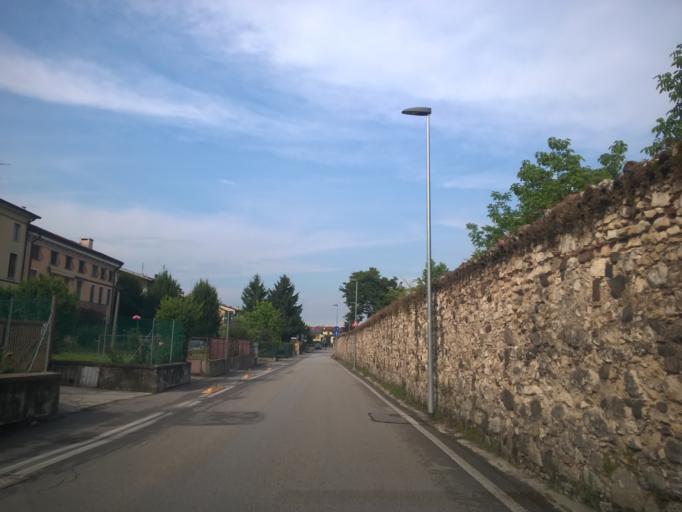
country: IT
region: Veneto
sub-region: Provincia di Vicenza
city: Malo
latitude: 45.6579
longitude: 11.4095
